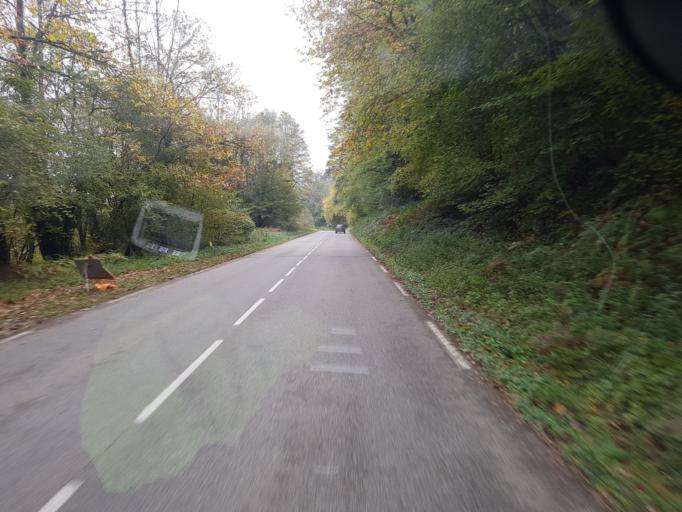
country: FR
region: Rhone-Alpes
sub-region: Departement de la Savoie
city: Saint-Genix-sur-Guiers
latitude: 45.6163
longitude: 5.6598
